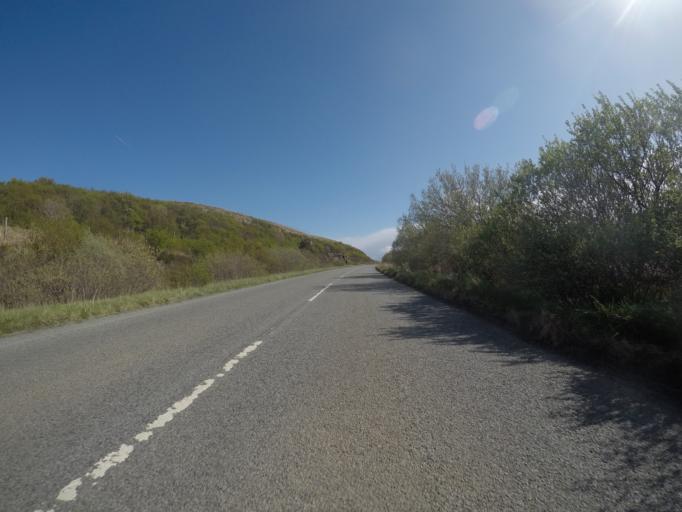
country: GB
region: Scotland
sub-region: Highland
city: Portree
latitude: 57.6066
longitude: -6.1722
